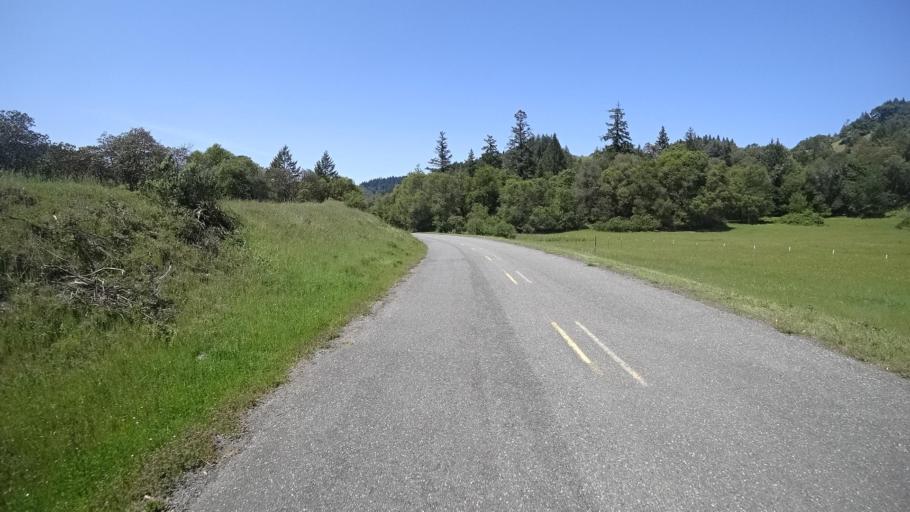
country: US
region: California
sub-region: Humboldt County
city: Redway
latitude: 40.2214
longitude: -123.6348
